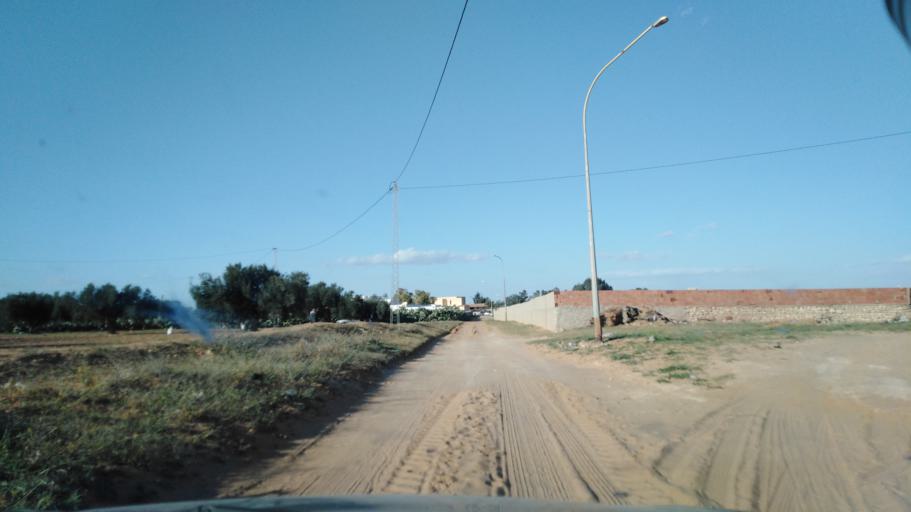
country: TN
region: Al Mahdiyah
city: Shurban
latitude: 34.9573
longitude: 10.3631
